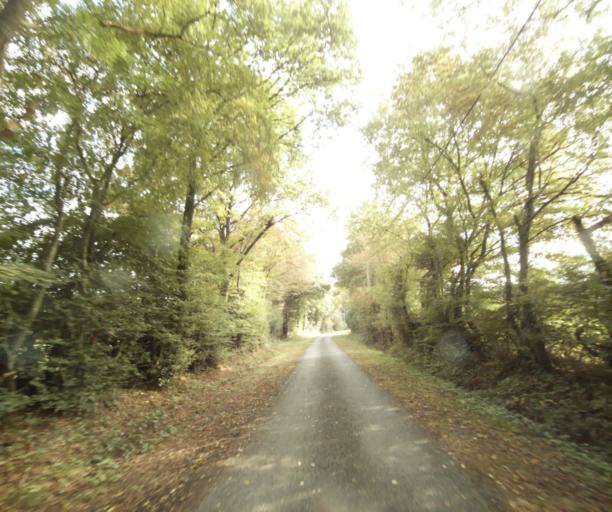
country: FR
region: Bourgogne
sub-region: Departement de Saone-et-Loire
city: Palinges
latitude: 46.5229
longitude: 4.2461
